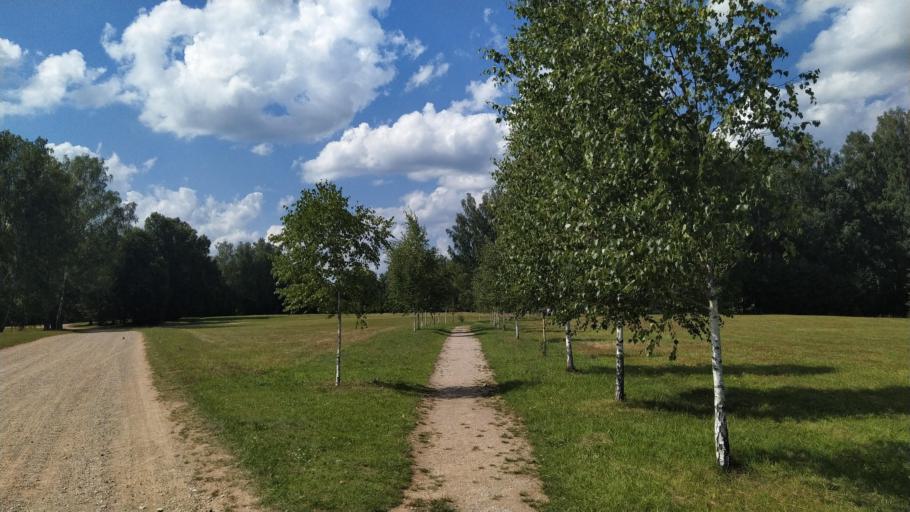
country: RU
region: Pskov
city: Pushkinskiye Gory
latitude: 57.0599
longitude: 28.9272
